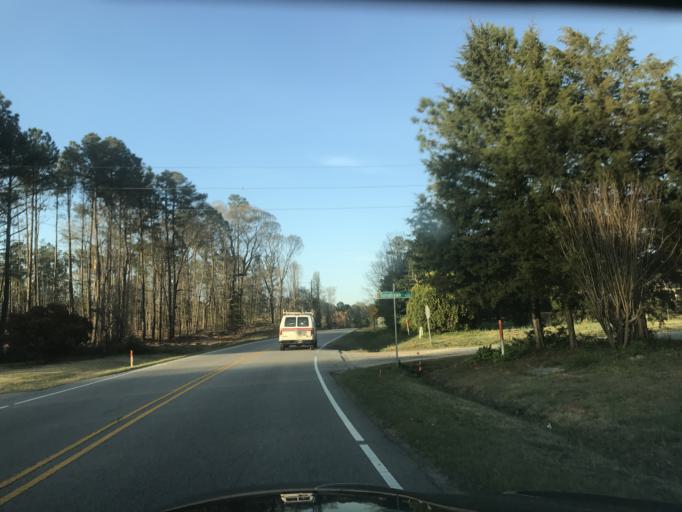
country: US
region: North Carolina
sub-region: Wake County
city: Garner
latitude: 35.7359
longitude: -78.5529
